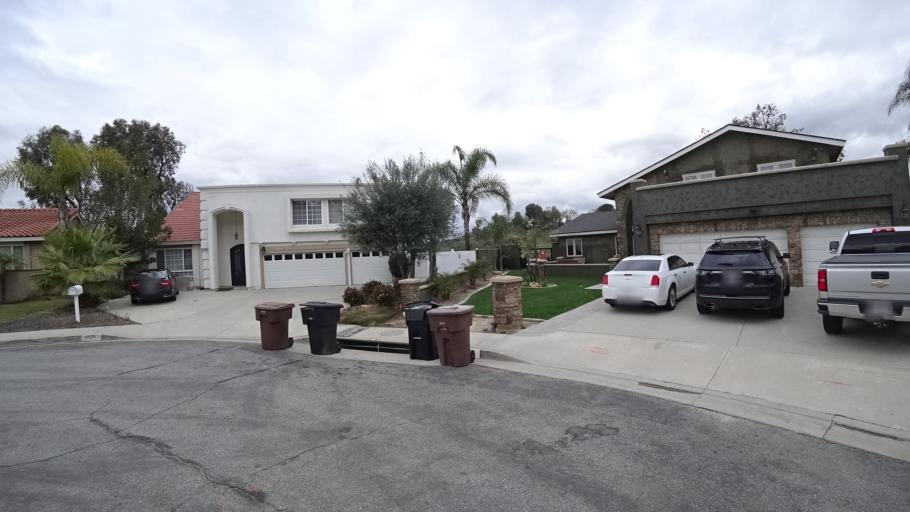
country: US
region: California
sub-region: Orange County
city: Villa Park
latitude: 33.8364
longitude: -117.7504
